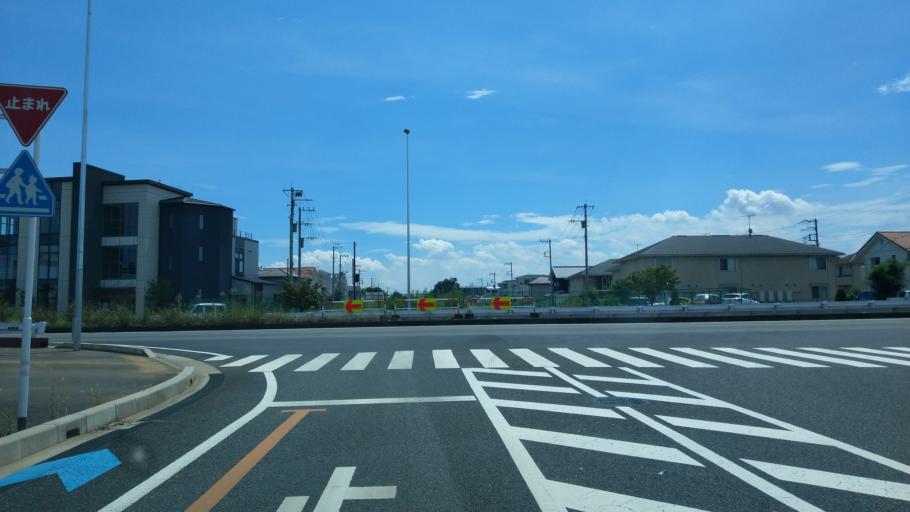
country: JP
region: Saitama
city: Ageoshimo
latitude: 35.9245
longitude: 139.5762
